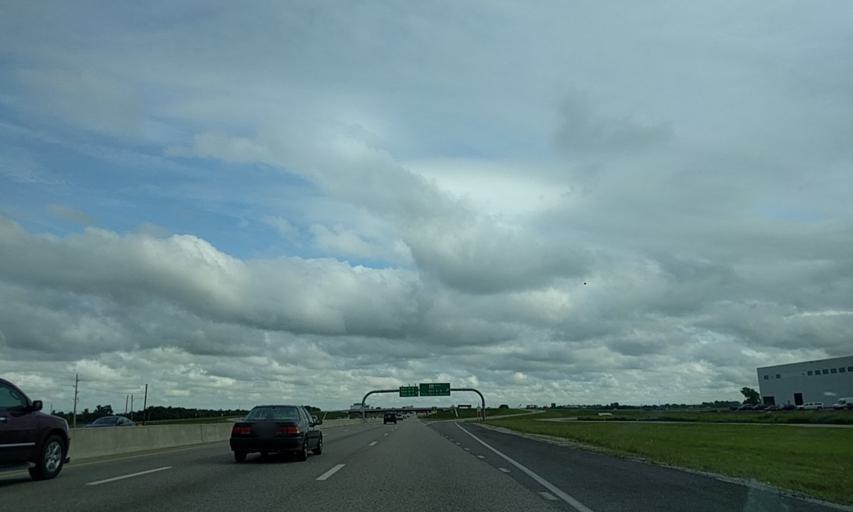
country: US
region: Oklahoma
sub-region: Tulsa County
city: Owasso
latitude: 36.2160
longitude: -95.8516
